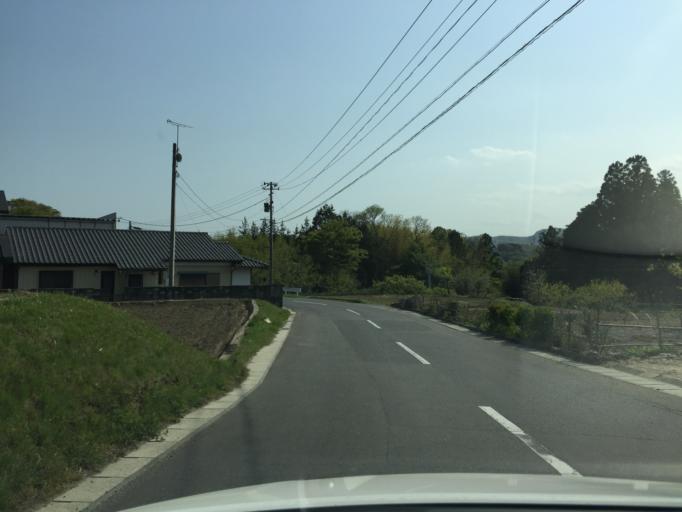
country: JP
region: Fukushima
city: Iwaki
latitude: 37.1306
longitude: 140.8698
